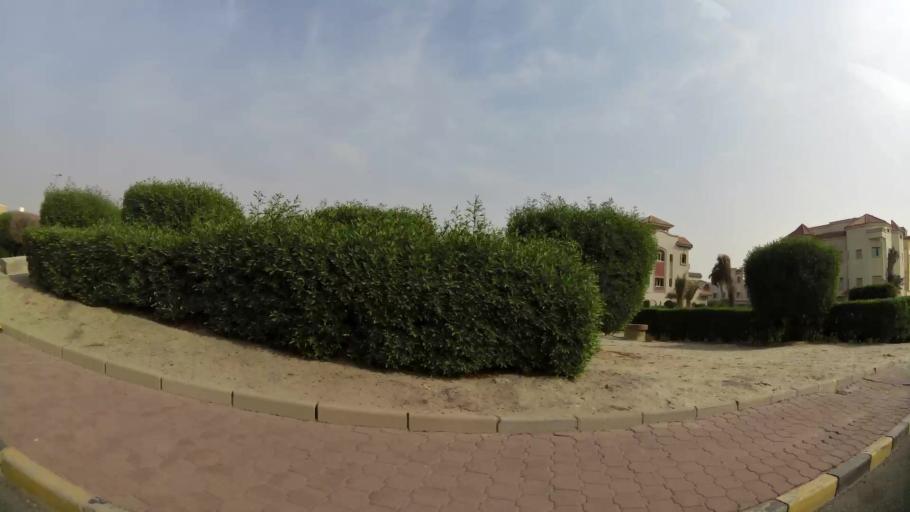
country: KW
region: Al Asimah
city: Ar Rabiyah
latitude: 29.2798
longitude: 47.9274
